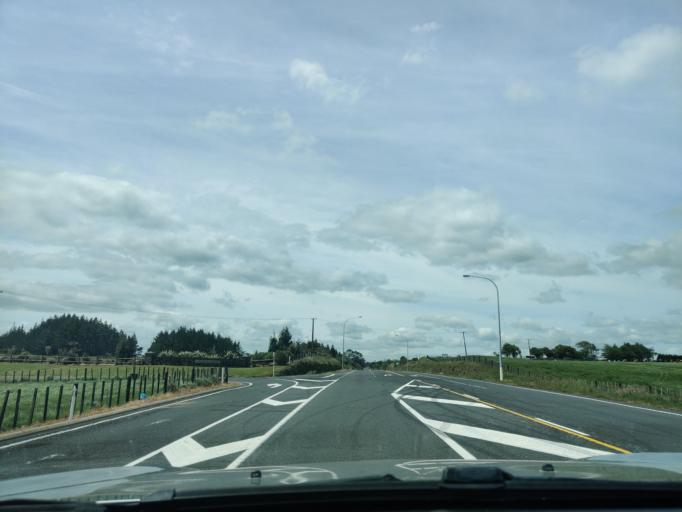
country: NZ
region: Taranaki
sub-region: New Plymouth District
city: New Plymouth
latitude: -39.1348
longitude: 174.1262
